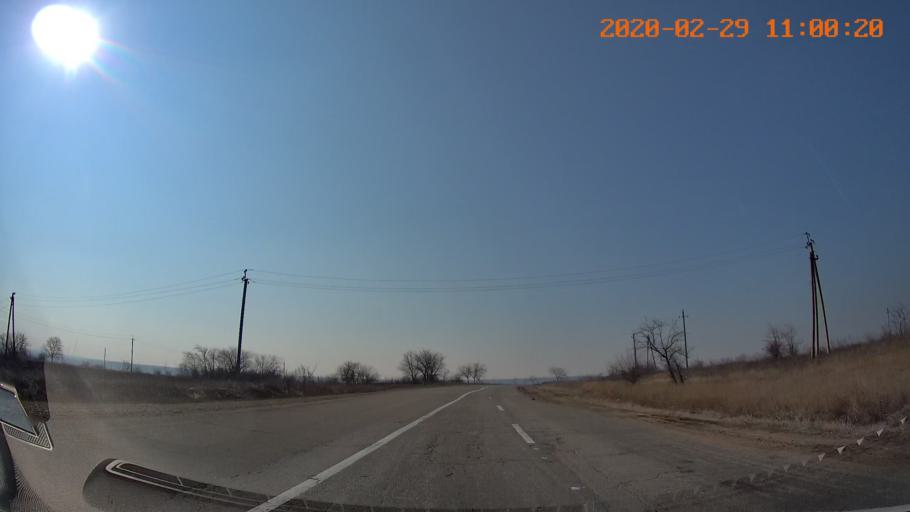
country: MD
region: Telenesti
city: Grigoriopol
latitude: 47.1627
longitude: 29.2791
